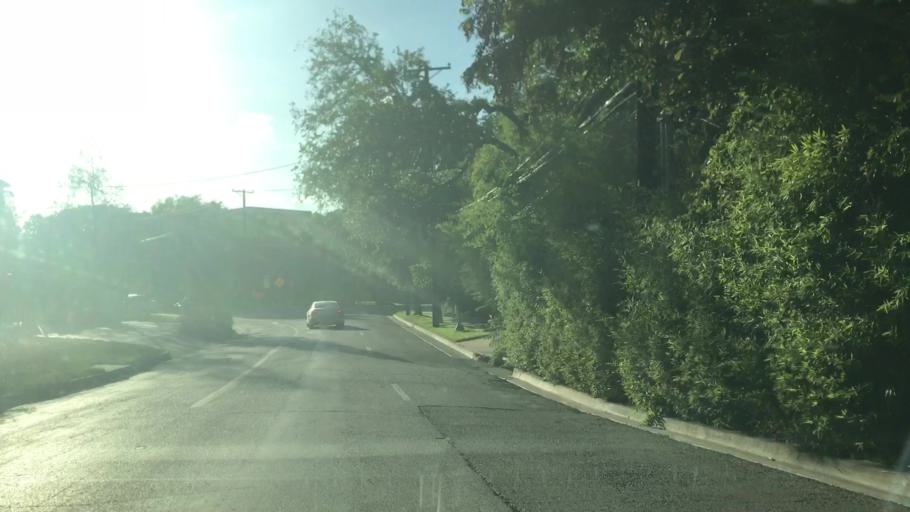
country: US
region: Texas
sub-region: Dallas County
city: Highland Park
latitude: 32.8193
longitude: -96.7987
